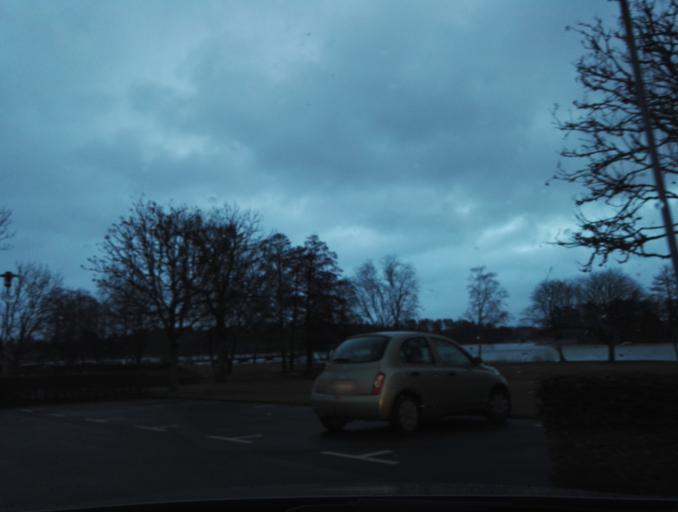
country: SE
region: Kronoberg
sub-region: Vaxjo Kommun
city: Vaexjoe
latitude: 56.9076
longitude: 14.7411
